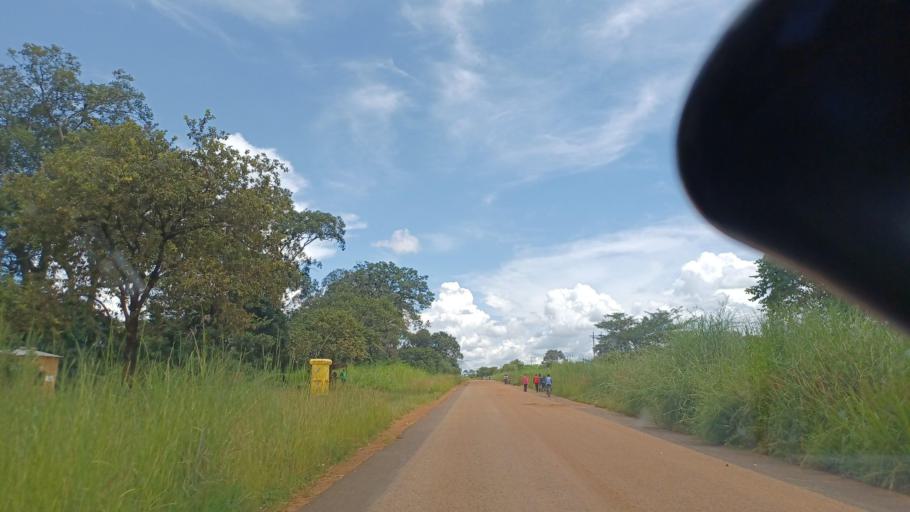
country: ZM
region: North-Western
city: Solwezi
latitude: -12.5571
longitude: 26.1442
